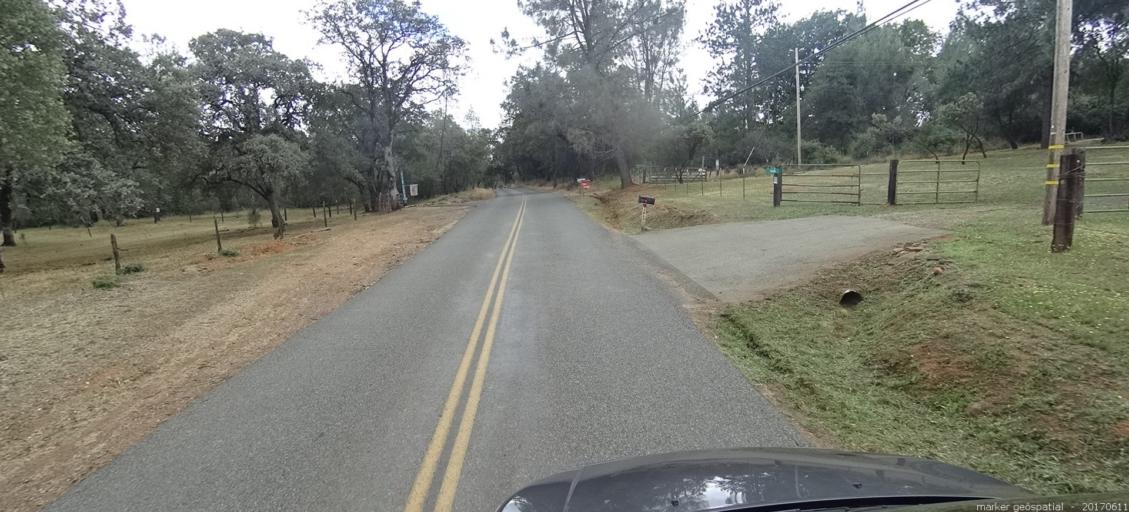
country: US
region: California
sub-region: Butte County
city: Oroville
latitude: 39.6261
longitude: -121.5285
